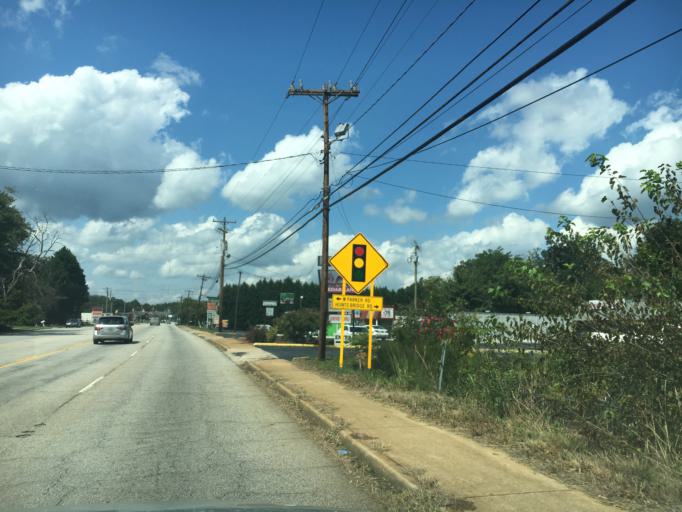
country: US
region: South Carolina
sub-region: Greenville County
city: Berea
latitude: 34.8823
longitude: -82.4521
